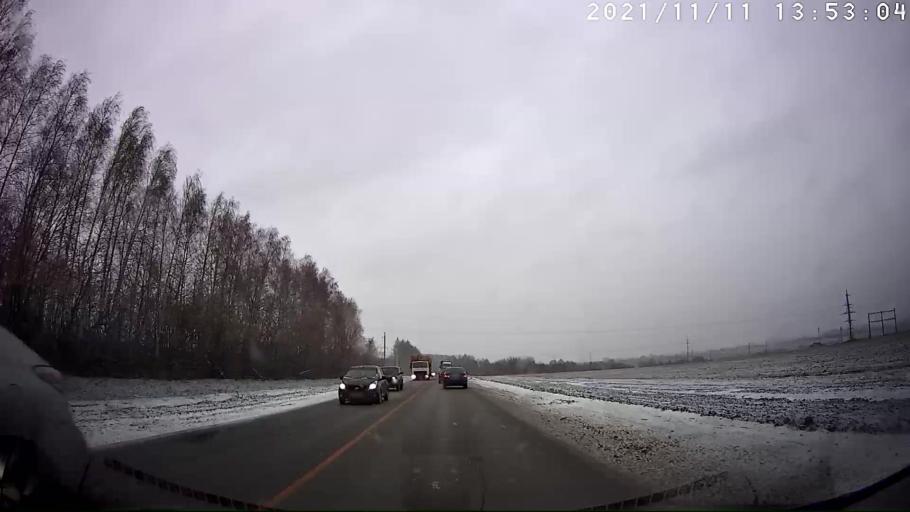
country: RU
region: Chuvashia
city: Shikhazany
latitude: 55.5743
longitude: 47.4127
